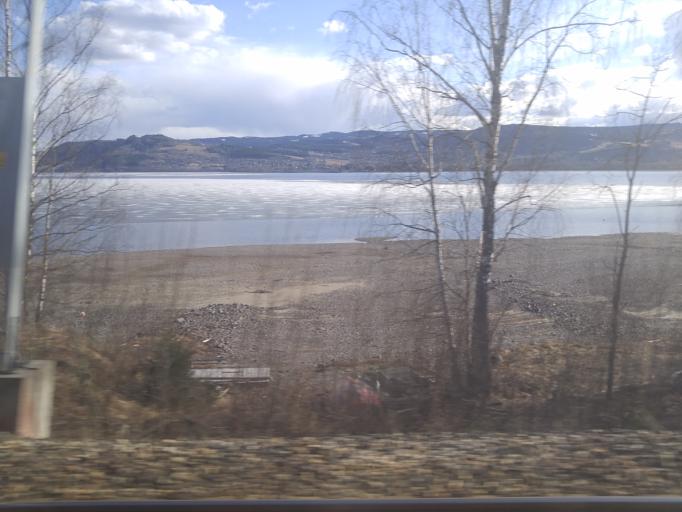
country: NO
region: Hedmark
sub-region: Ringsaker
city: Moelv
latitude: 60.9819
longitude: 10.6435
